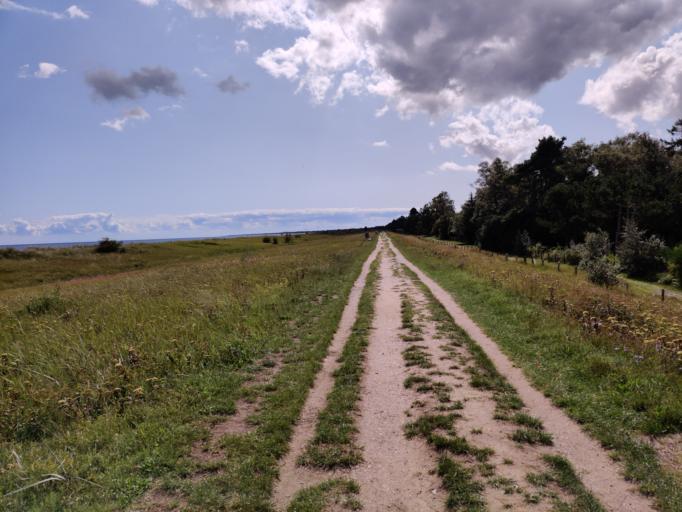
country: DK
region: Zealand
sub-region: Guldborgsund Kommune
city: Nykobing Falster
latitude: 54.6939
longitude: 11.9714
